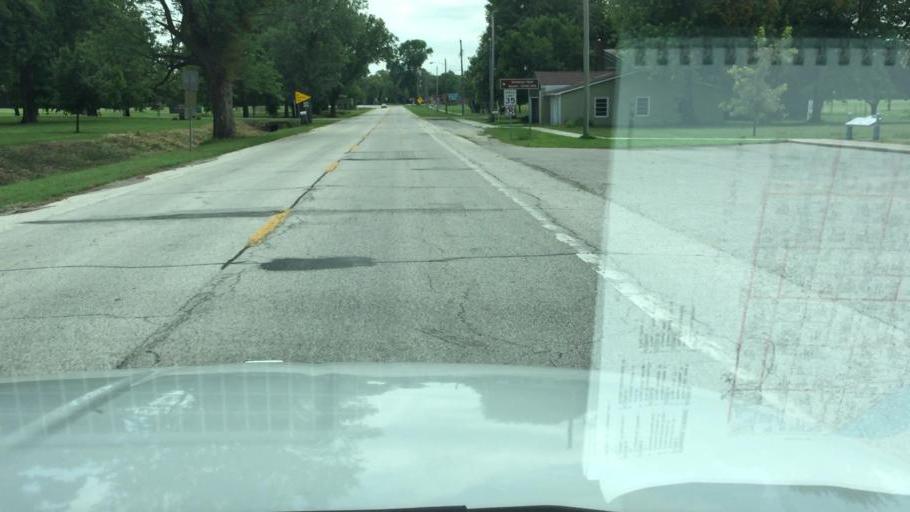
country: US
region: Illinois
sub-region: Hancock County
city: Nauvoo
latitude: 40.5440
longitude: -91.3866
